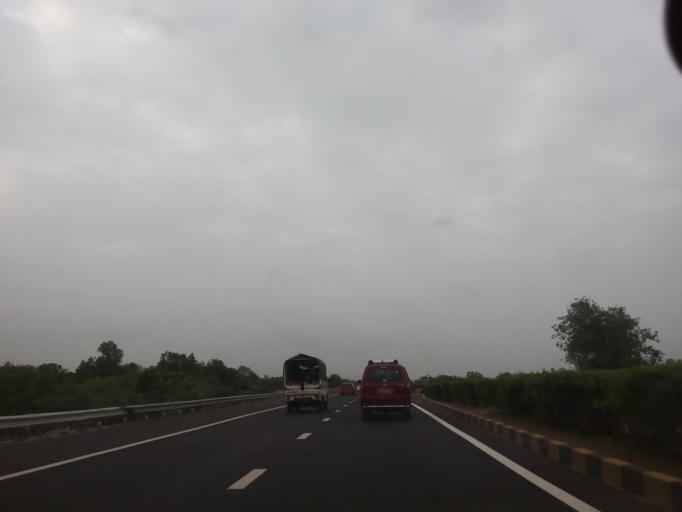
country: IN
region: Gujarat
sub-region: Kheda
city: Mahemdavad
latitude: 22.7905
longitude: 72.8427
